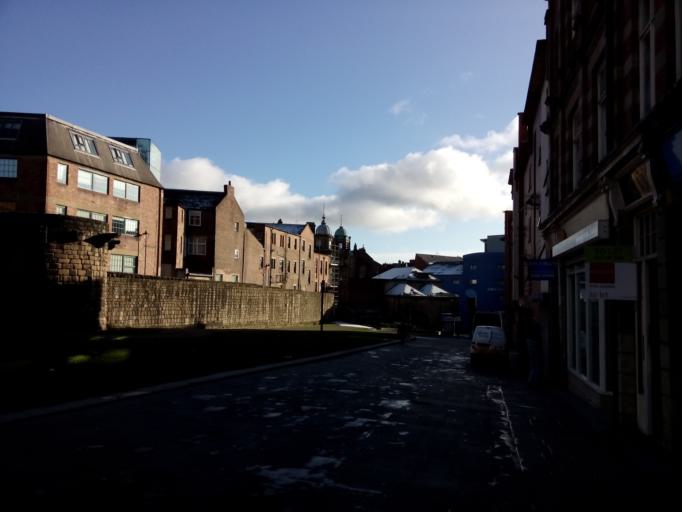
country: GB
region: England
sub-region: Newcastle upon Tyne
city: Newcastle upon Tyne
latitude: 54.9713
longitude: -1.6213
